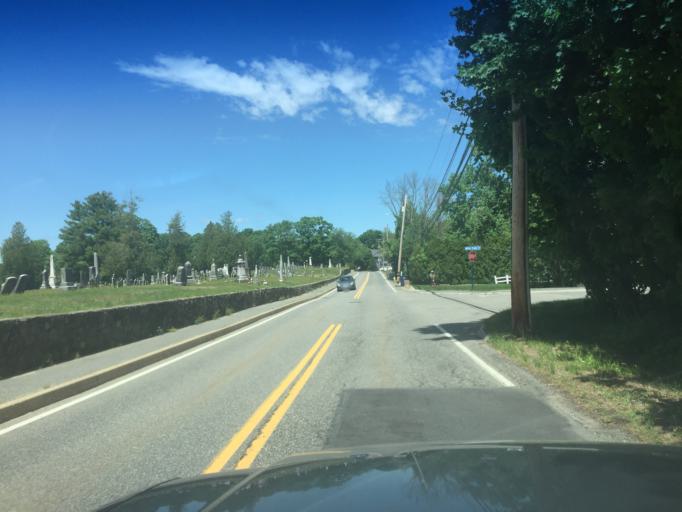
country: US
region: Massachusetts
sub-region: Norfolk County
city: Medway
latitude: 42.1456
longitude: -71.4220
